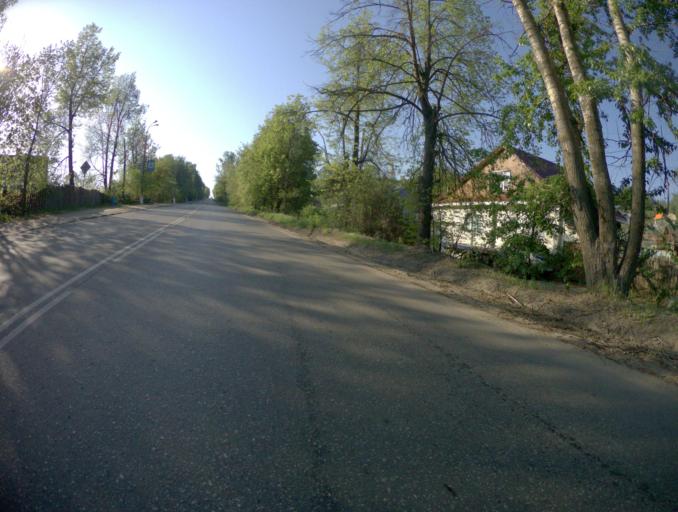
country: RU
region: Vladimir
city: Vyazniki
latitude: 56.2448
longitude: 42.1627
